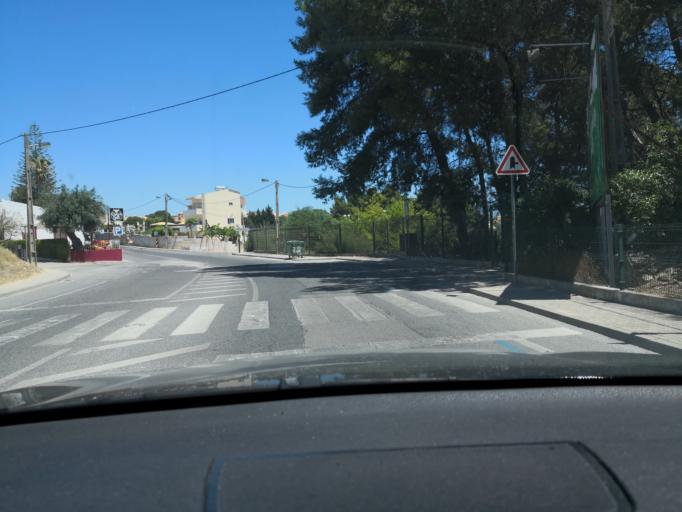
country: PT
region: Faro
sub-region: Albufeira
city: Albufeira
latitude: 37.0994
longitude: -8.2172
